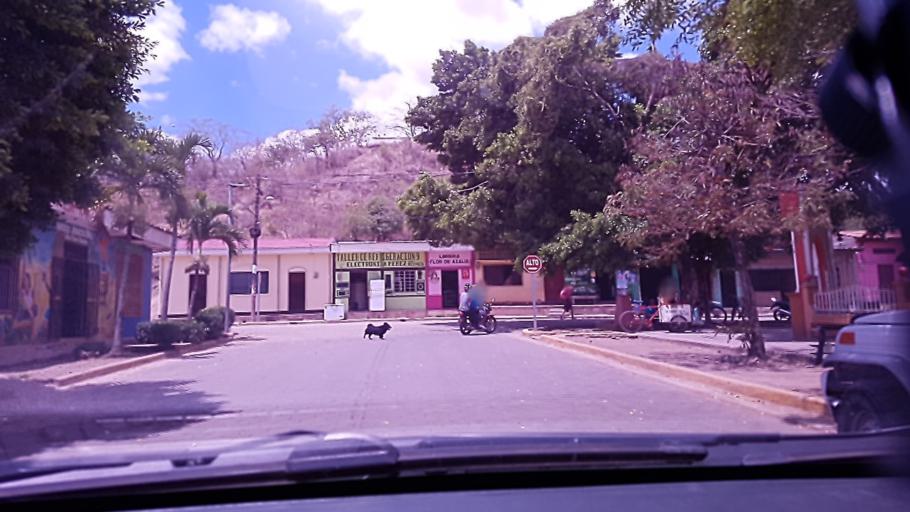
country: NI
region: Esteli
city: Condega
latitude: 13.3603
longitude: -86.3983
